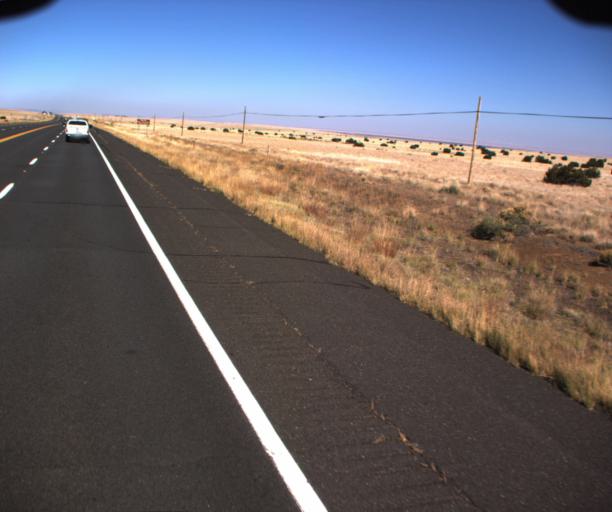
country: US
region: Arizona
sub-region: Coconino County
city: Flagstaff
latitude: 35.5698
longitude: -111.5320
